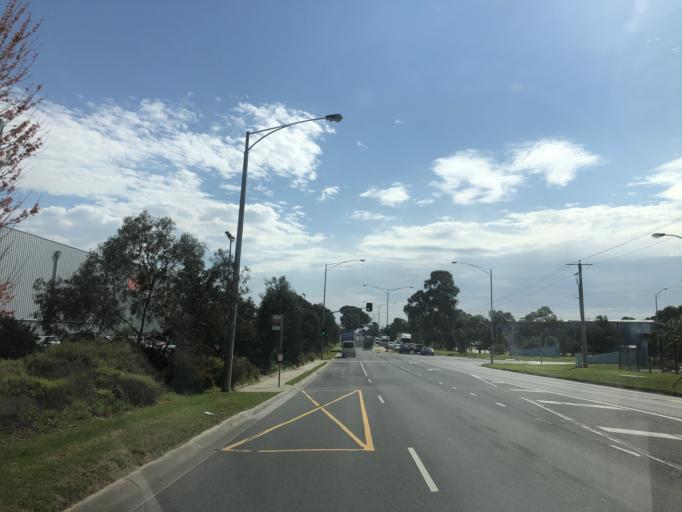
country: AU
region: Victoria
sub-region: Casey
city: Hampton Park
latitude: -38.0338
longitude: 145.2285
